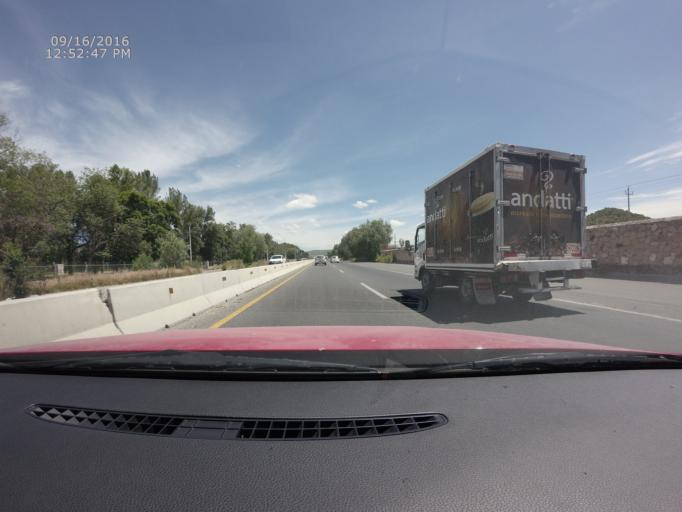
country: MX
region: Queretaro
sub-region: Colon
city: Purisima de Cubos (La Purisima)
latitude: 20.6191
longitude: -100.1377
